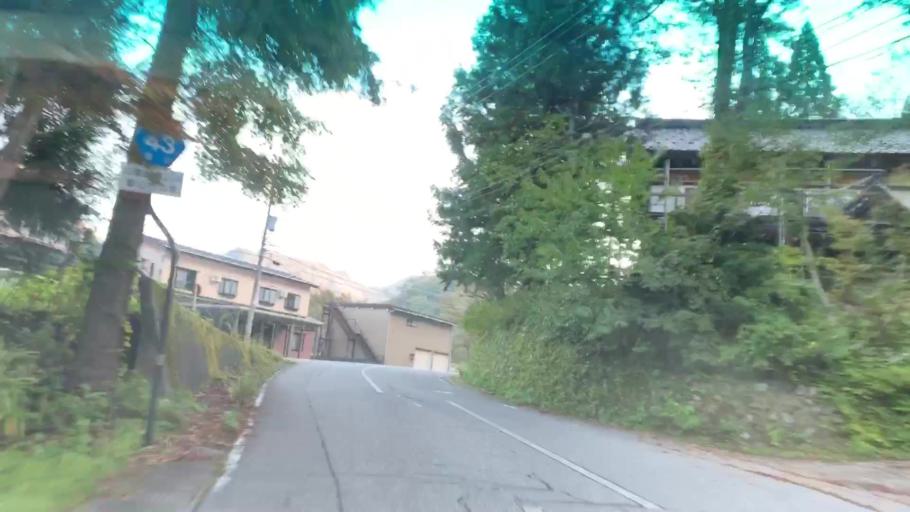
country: JP
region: Toyama
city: Kamiichi
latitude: 36.5721
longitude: 137.3840
